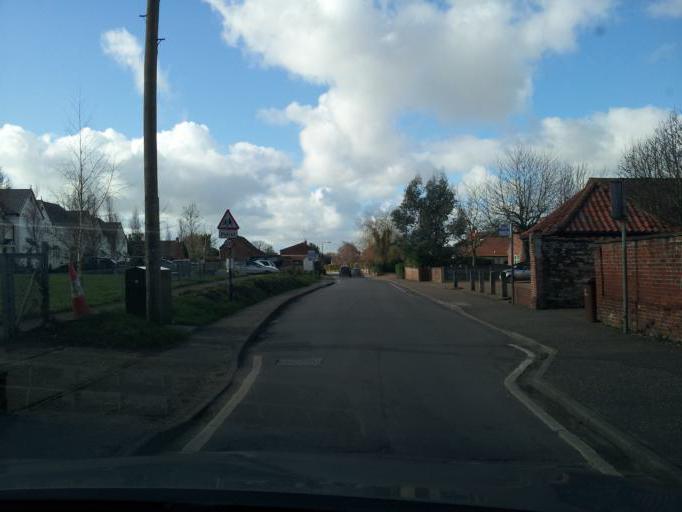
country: GB
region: England
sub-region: Norfolk
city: Mattishall
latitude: 52.6588
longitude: 1.0339
